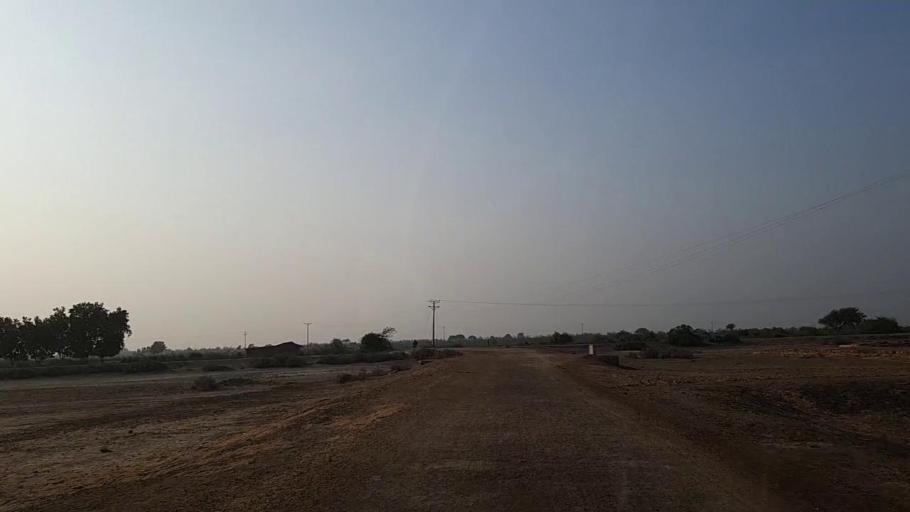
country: PK
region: Sindh
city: Thatta
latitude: 24.6938
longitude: 67.7856
